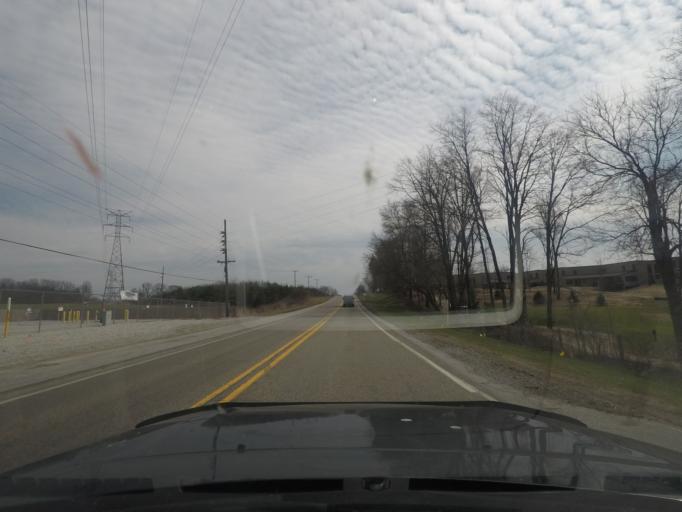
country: US
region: Indiana
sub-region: LaPorte County
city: LaPorte
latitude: 41.6492
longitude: -86.7560
